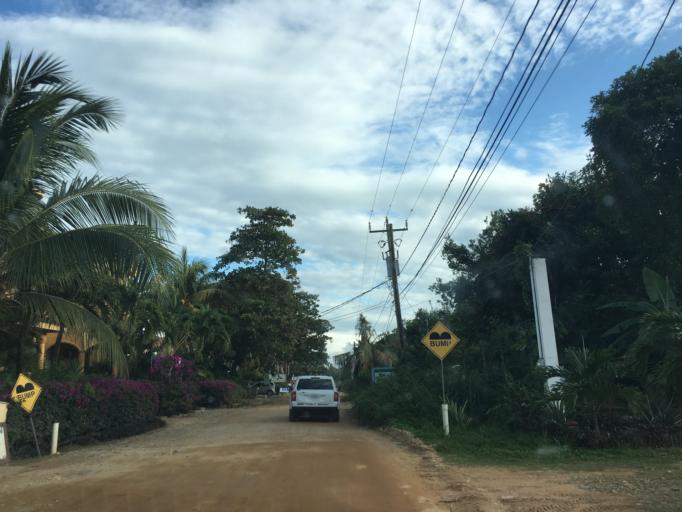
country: BZ
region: Stann Creek
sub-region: Dangriga
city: Dangriga
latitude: 16.8390
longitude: -88.2707
